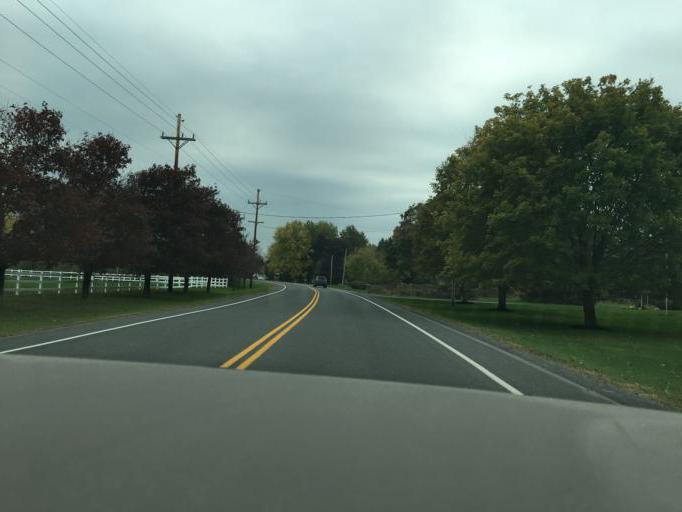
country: US
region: New York
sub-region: Ontario County
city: Victor
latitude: 42.9799
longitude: -77.3255
